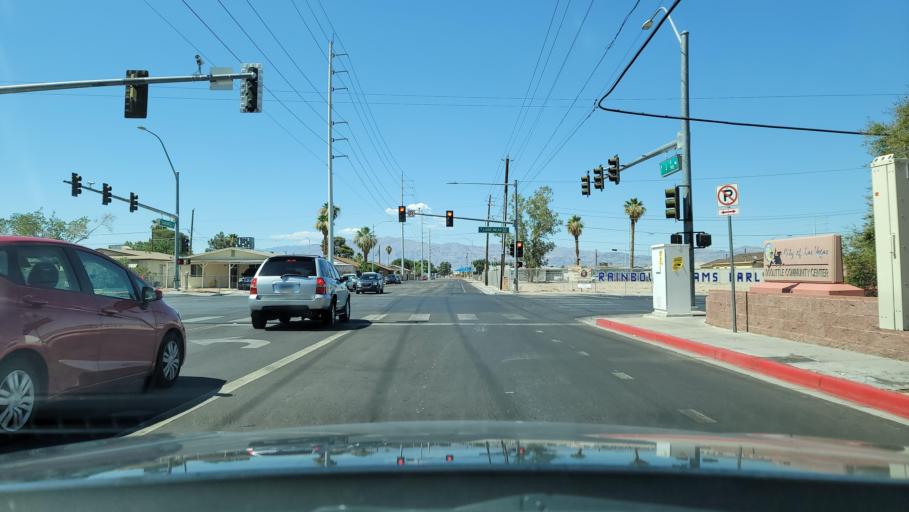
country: US
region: Nevada
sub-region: Clark County
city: Las Vegas
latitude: 36.1953
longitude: -115.1563
